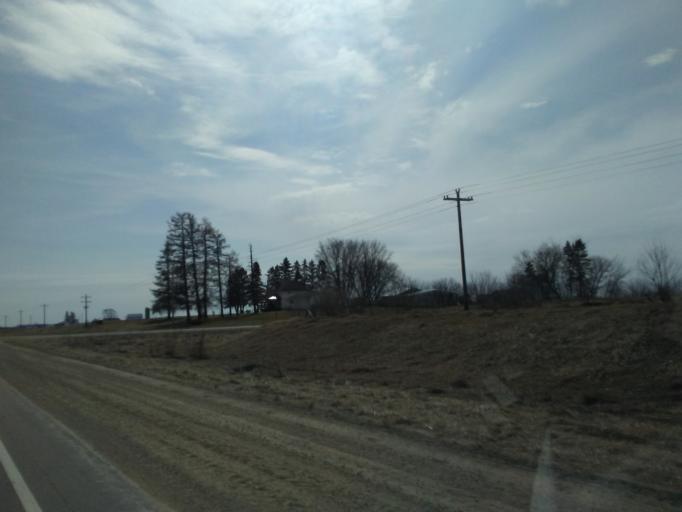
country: US
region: Iowa
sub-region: Winneshiek County
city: Decorah
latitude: 43.4440
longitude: -91.8621
